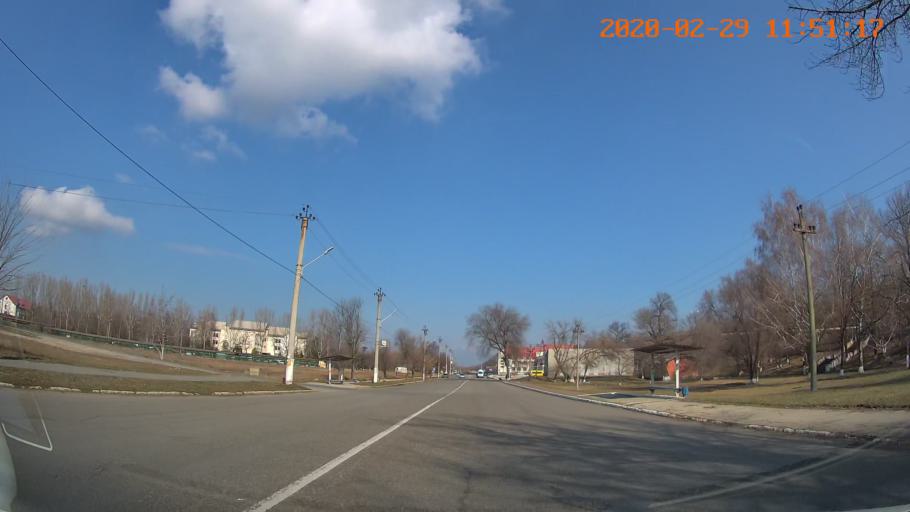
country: MD
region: Telenesti
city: Ribnita
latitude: 47.7642
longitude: 28.9898
